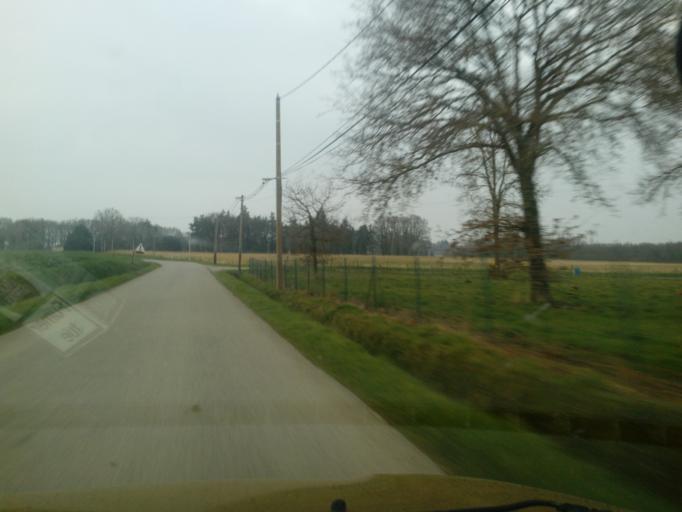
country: FR
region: Brittany
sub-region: Departement du Morbihan
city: Guilliers
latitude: 48.0509
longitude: -2.4019
